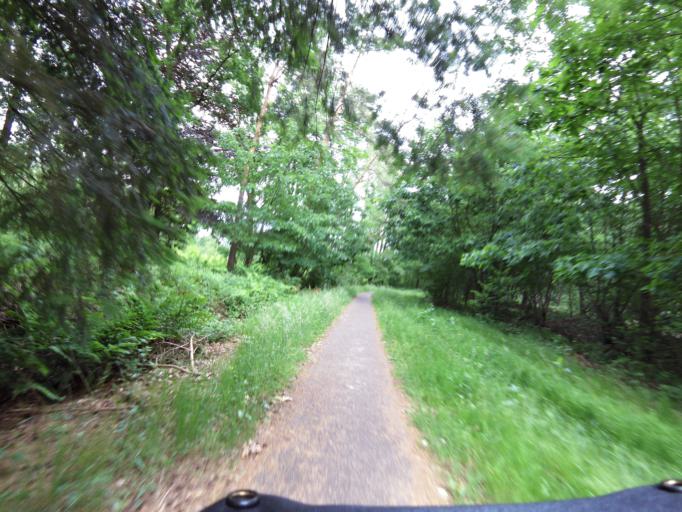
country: NL
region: North Brabant
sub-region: Gemeente Breda
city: Breda
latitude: 51.5453
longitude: 4.8290
